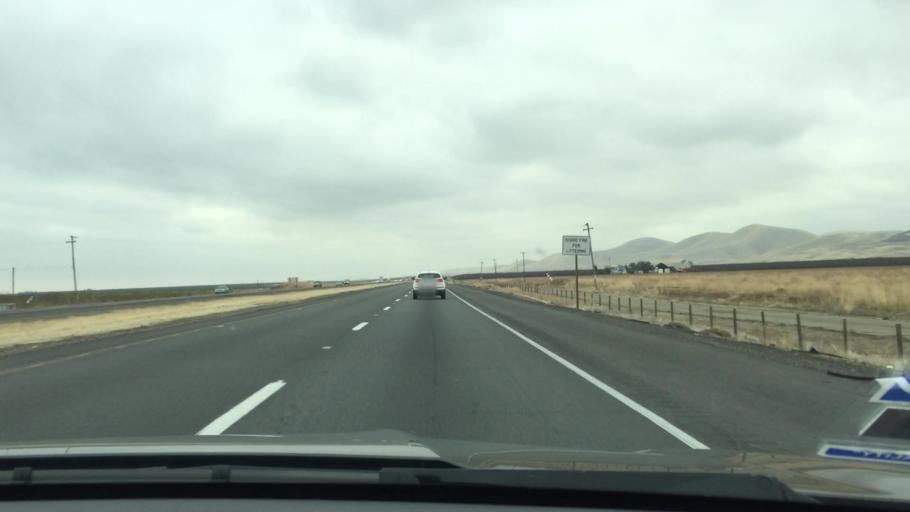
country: US
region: California
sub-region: Merced County
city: Gustine
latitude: 37.2374
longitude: -121.0869
